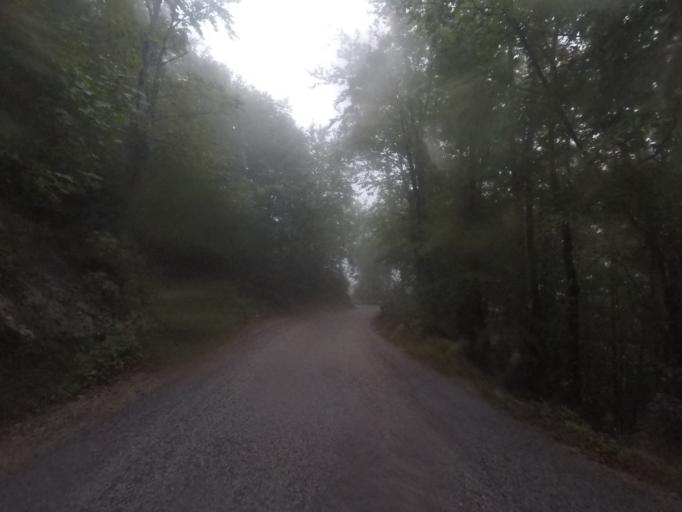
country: HR
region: Licko-Senjska
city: Jezerce
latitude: 44.9285
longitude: 15.5567
